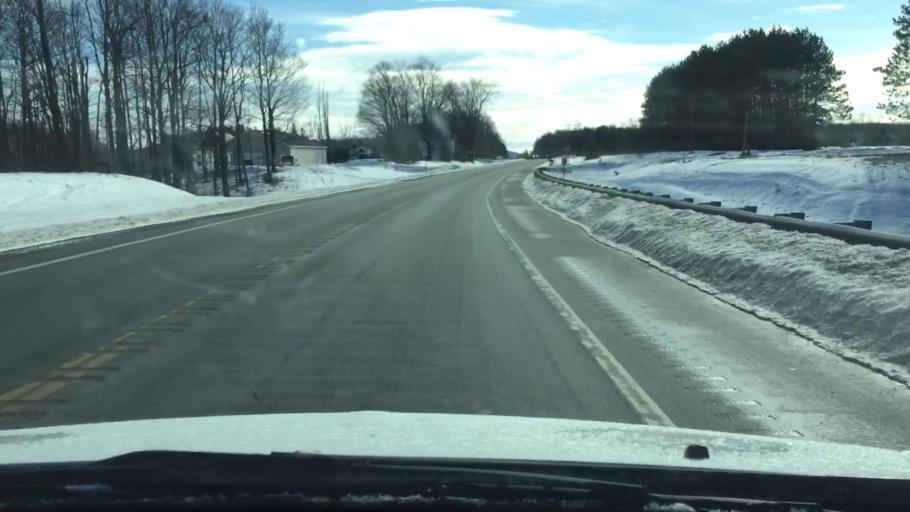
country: US
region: Michigan
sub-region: Antrim County
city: Mancelona
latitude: 44.9452
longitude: -85.0506
